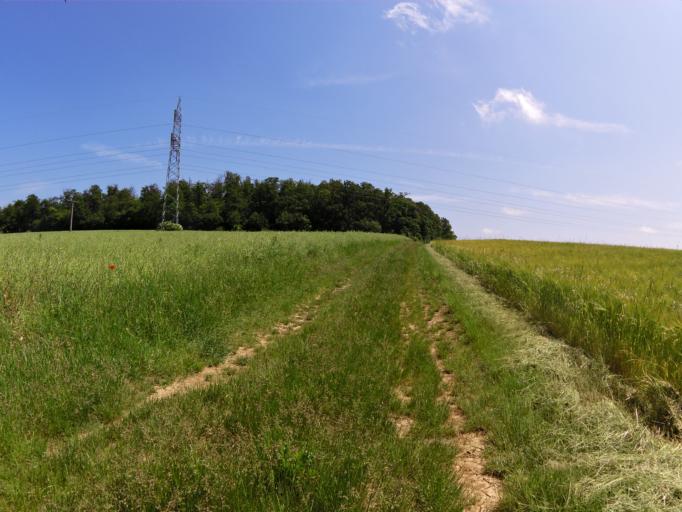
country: DE
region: Bavaria
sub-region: Regierungsbezirk Unterfranken
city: Kleinrinderfeld
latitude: 49.7170
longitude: 9.8426
